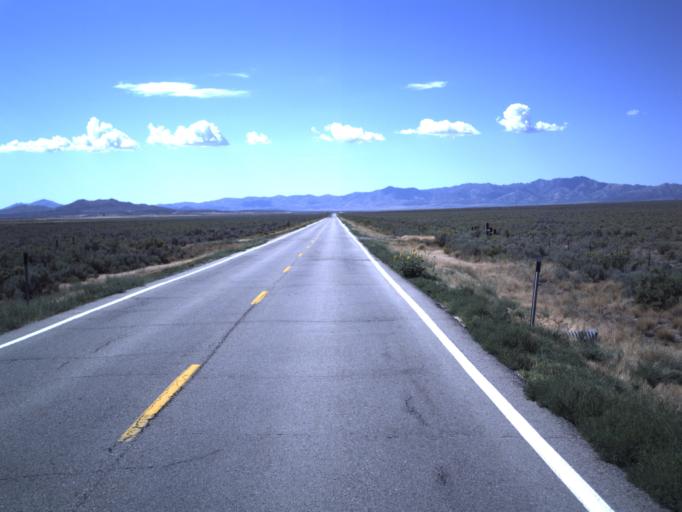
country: US
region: Utah
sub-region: Tooele County
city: Tooele
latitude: 40.2464
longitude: -112.4003
